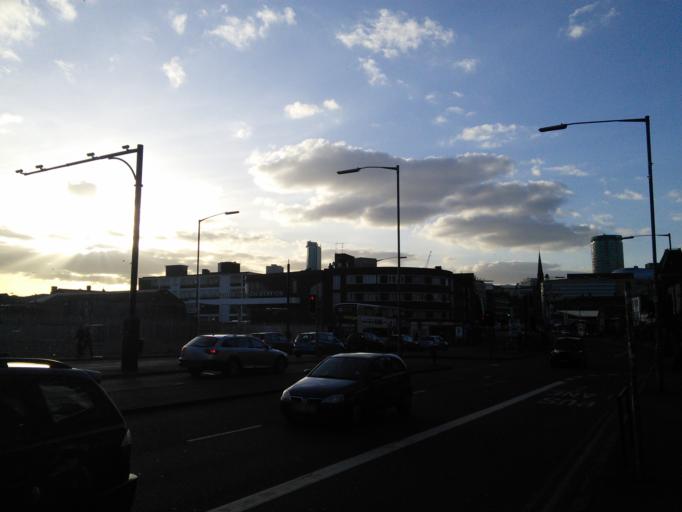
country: GB
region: England
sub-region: City and Borough of Birmingham
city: Birmingham
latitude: 52.4751
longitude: -1.8865
